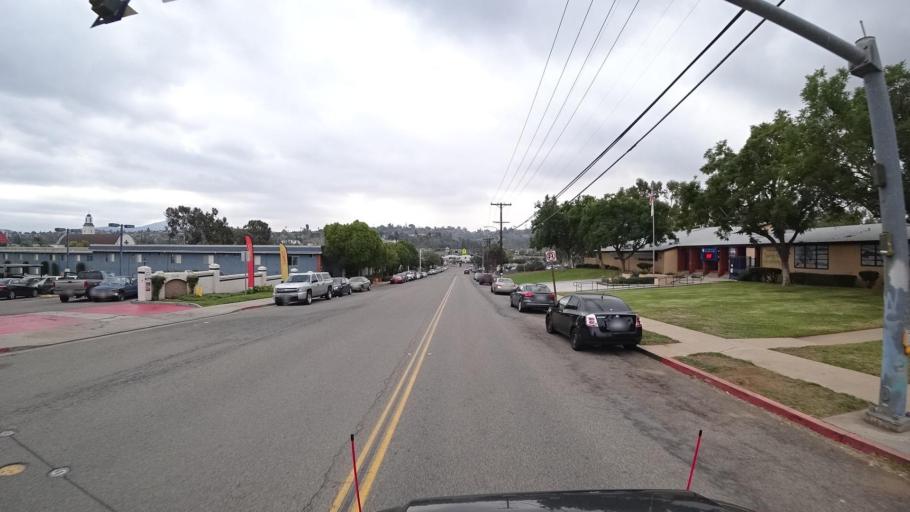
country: US
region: California
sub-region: San Diego County
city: Spring Valley
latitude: 32.7507
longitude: -116.9873
